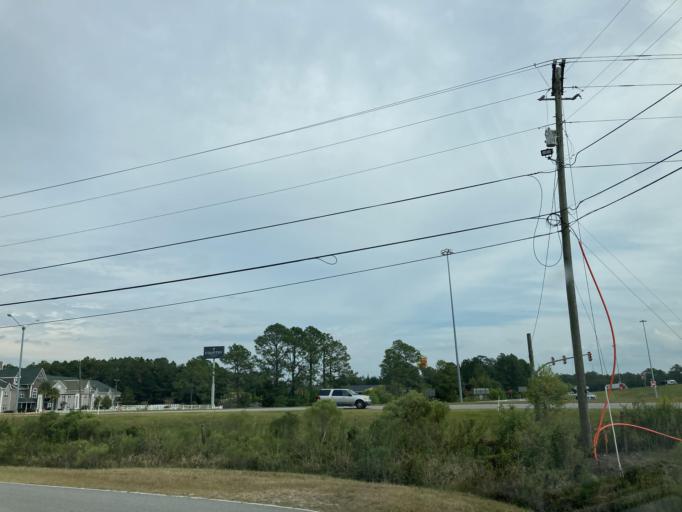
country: US
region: Mississippi
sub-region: Jackson County
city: Gulf Hills
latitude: 30.4558
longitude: -88.8437
